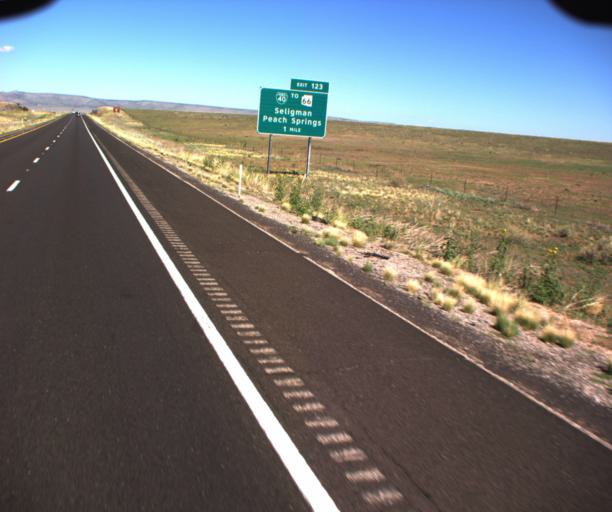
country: US
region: Arizona
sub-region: Yavapai County
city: Paulden
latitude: 35.3001
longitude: -112.8375
